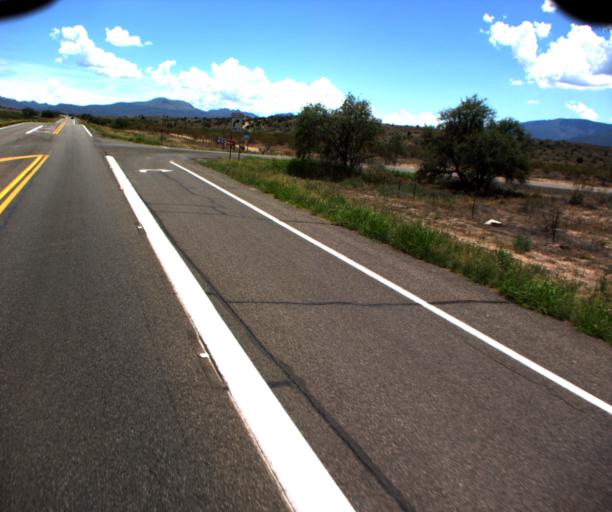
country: US
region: Arizona
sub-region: Yavapai County
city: Camp Verde
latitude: 34.5414
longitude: -111.8244
